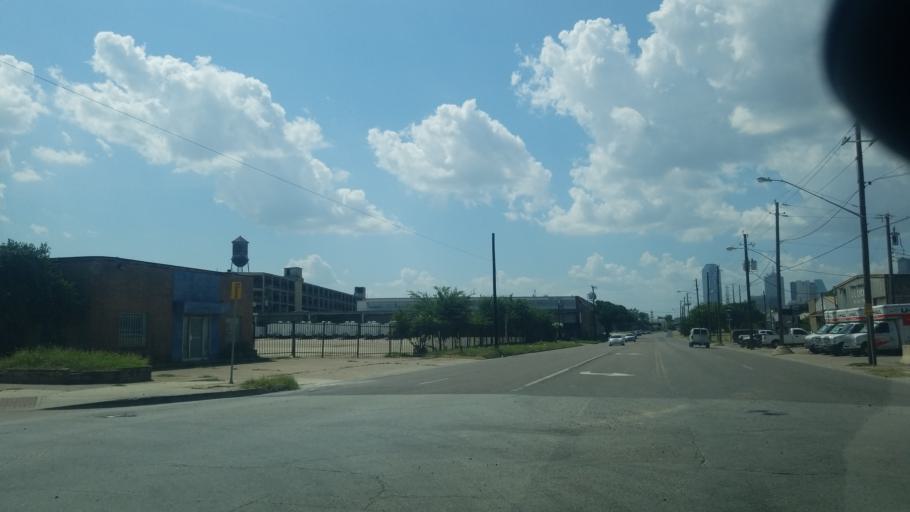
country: US
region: Texas
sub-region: Dallas County
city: Dallas
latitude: 32.7581
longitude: -96.7811
